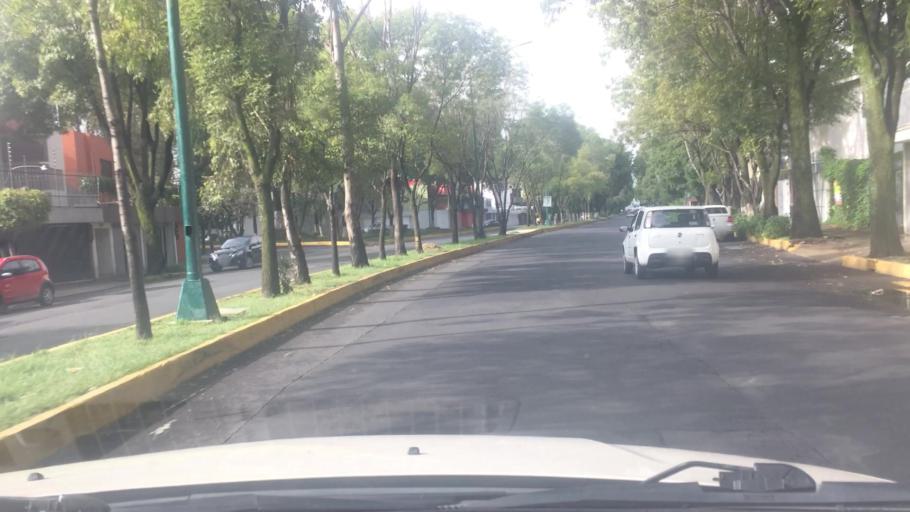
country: MX
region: Mexico City
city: Coyoacan
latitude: 19.3425
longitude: -99.1264
